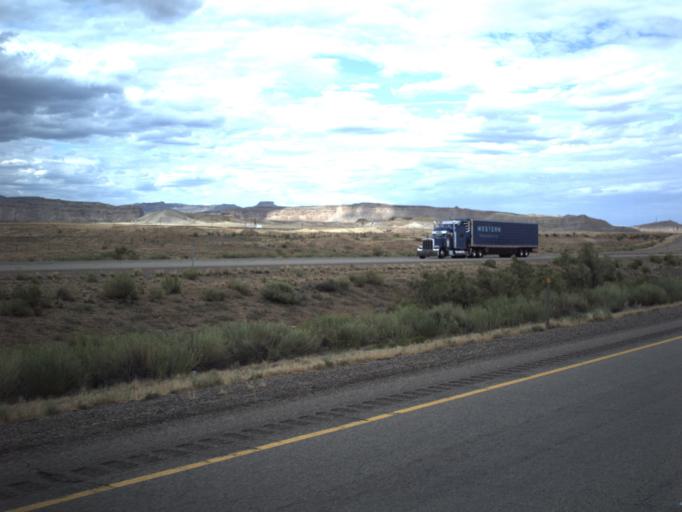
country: US
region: Utah
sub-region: Grand County
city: Moab
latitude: 38.9204
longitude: -109.9411
